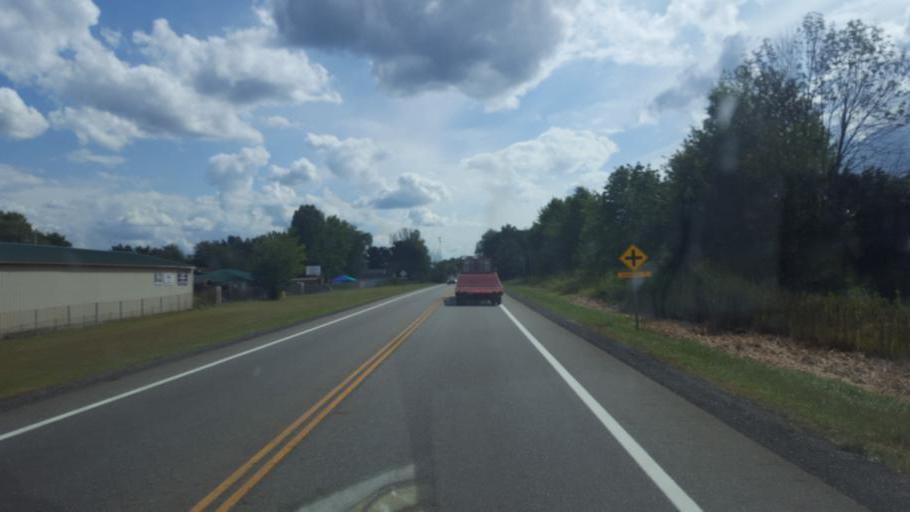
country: US
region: Ohio
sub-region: Portage County
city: Ravenna
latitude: 41.1630
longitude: -81.2199
